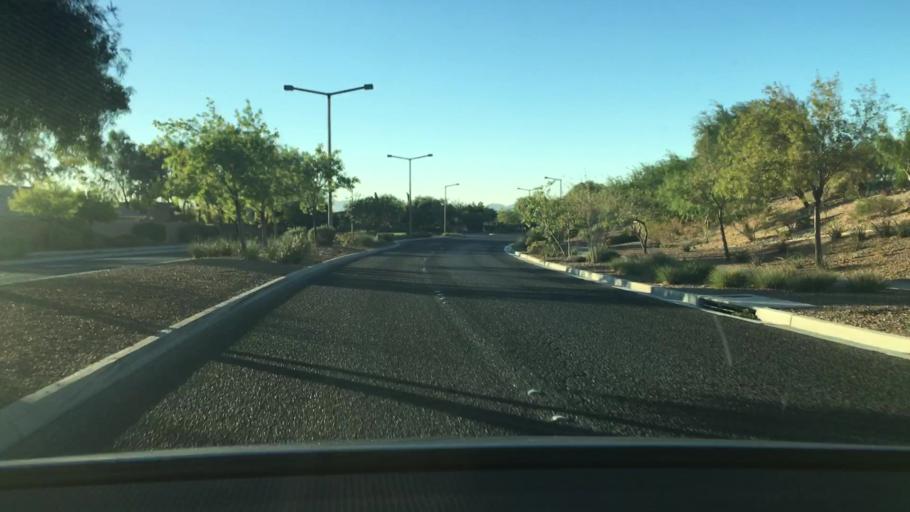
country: US
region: Nevada
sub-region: Clark County
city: Summerlin South
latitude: 36.1242
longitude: -115.3371
